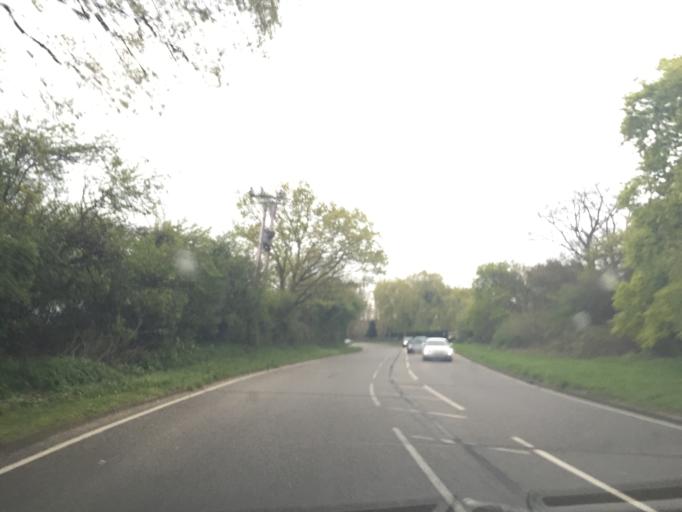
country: GB
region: England
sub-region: Essex
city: Theydon Bois
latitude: 51.6567
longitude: 0.1155
